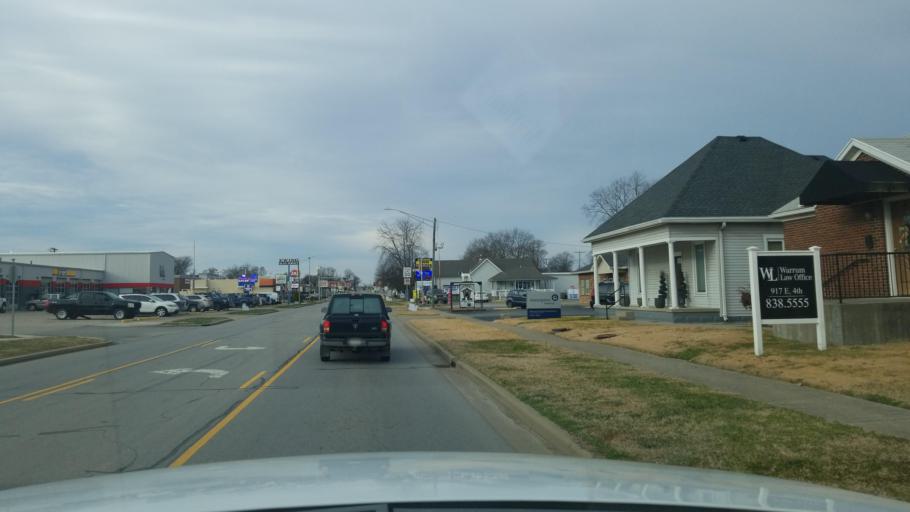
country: US
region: Indiana
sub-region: Posey County
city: Mount Vernon
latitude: 37.9348
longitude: -87.8855
